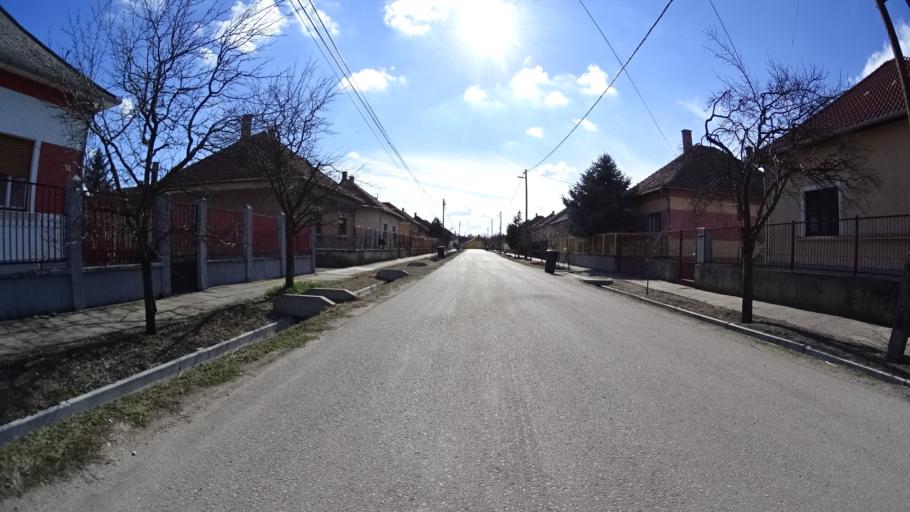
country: HU
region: Bacs-Kiskun
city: Tiszakecske
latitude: 46.9353
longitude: 20.1001
